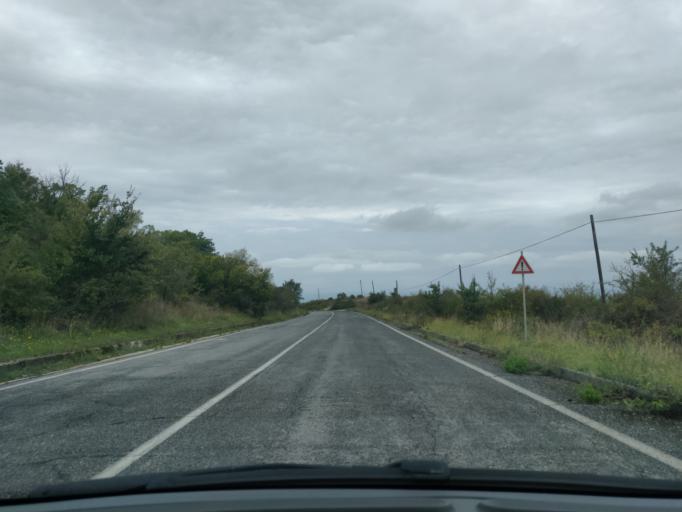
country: IT
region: Latium
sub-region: Citta metropolitana di Roma Capitale
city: Civitavecchia
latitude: 42.1122
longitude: 11.8478
